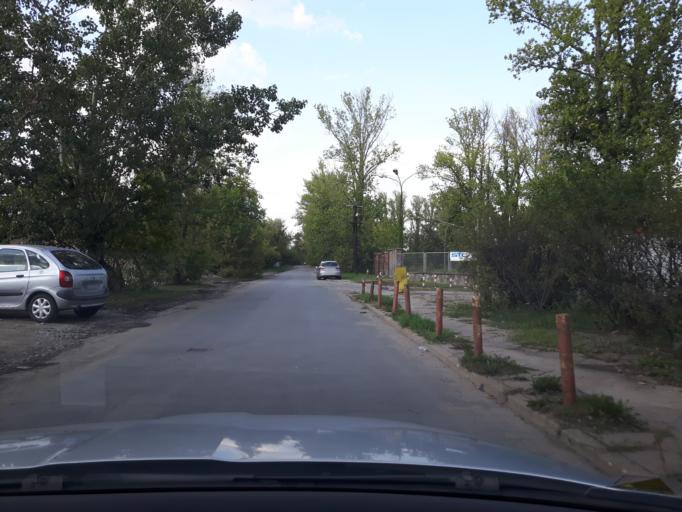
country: PL
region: Masovian Voivodeship
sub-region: Warszawa
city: Praga Poludnie
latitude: 52.2545
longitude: 21.0741
